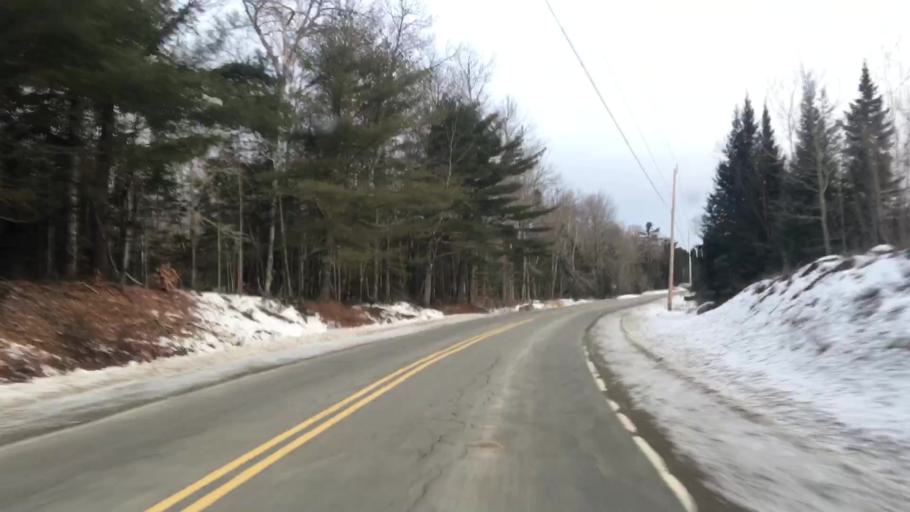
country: US
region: Maine
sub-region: Hancock County
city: Franklin
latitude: 44.7585
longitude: -68.3249
